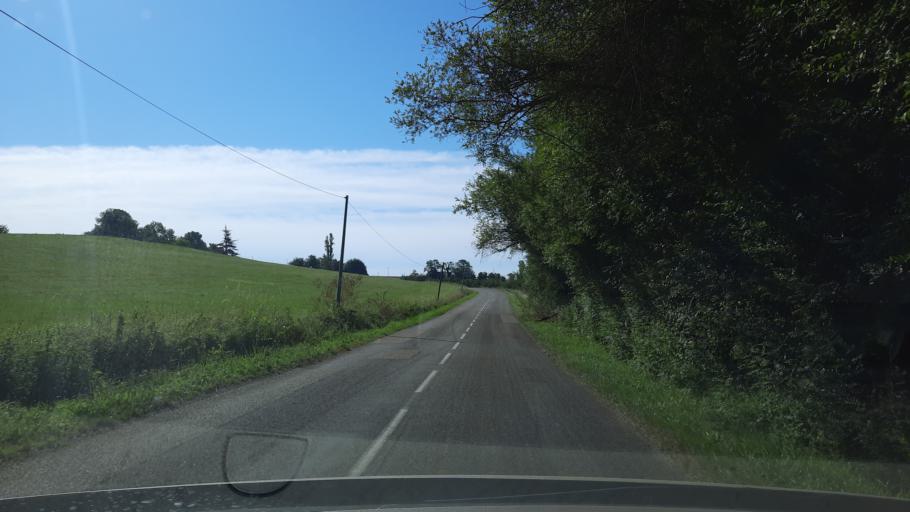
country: FR
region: Midi-Pyrenees
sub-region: Departement du Tarn-et-Garonne
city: Molieres
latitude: 44.1970
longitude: 1.4329
